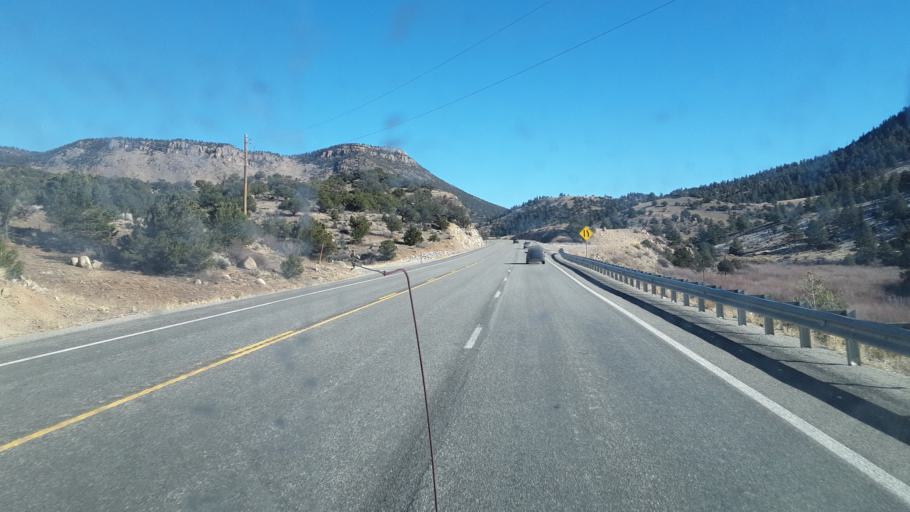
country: US
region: Colorado
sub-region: Chaffee County
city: Buena Vista
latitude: 38.8312
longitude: -106.0287
